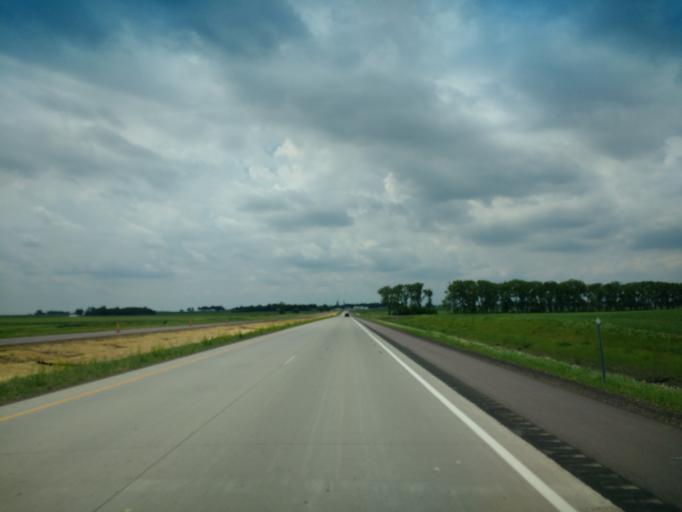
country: US
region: Minnesota
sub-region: Cottonwood County
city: Mountain Lake
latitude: 43.9149
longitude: -95.0142
